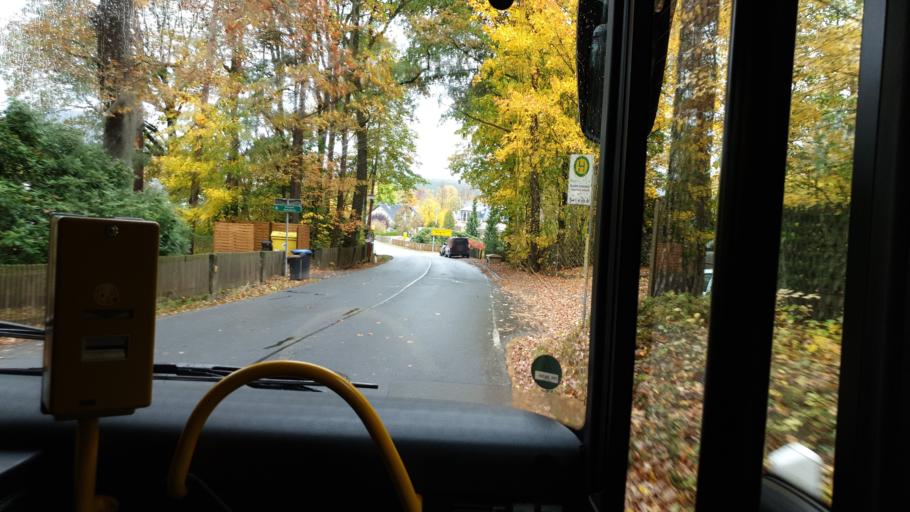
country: DE
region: Saxony
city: Kurort Gohrisch
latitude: 50.9086
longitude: 14.1095
